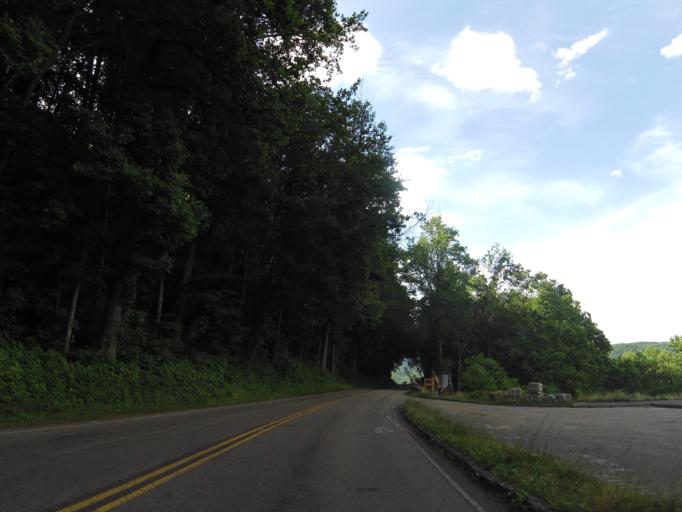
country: US
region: Tennessee
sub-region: Sevier County
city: Gatlinburg
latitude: 35.6581
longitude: -83.5201
